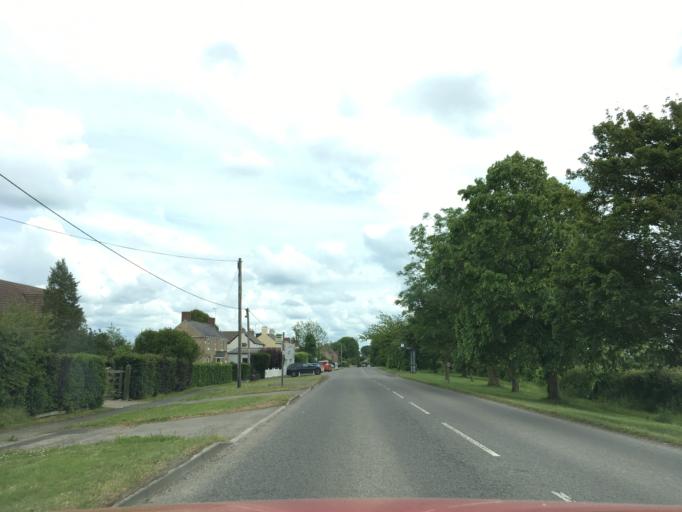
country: GB
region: England
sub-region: Wiltshire
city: Lyneham
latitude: 51.5599
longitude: -1.9880
